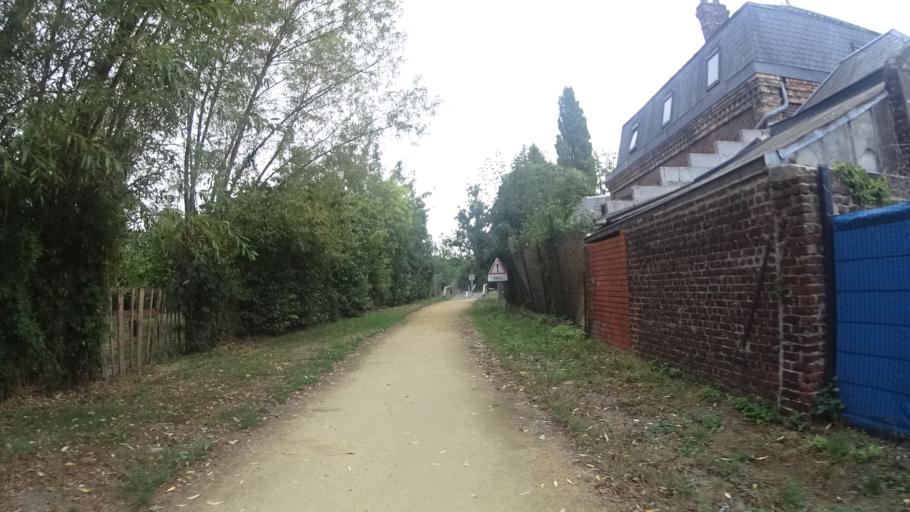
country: FR
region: Picardie
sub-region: Departement de l'Aisne
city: Origny-Sainte-Benoite
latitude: 49.8404
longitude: 3.4858
